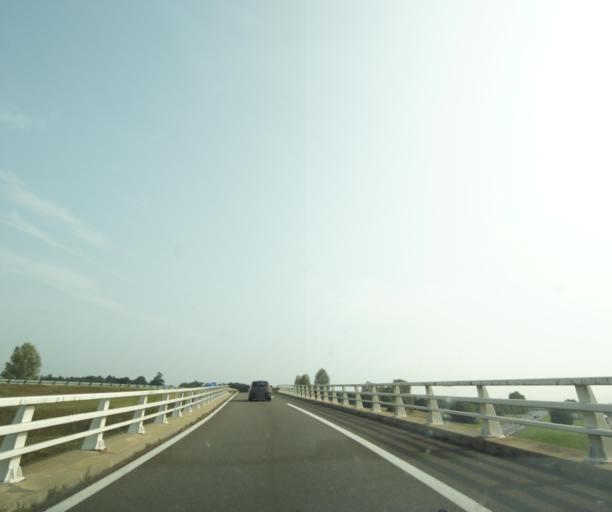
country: FR
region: Pays de la Loire
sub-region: Departement de la Sarthe
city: Saint-Saturnin
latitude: 48.0515
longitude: 0.1787
